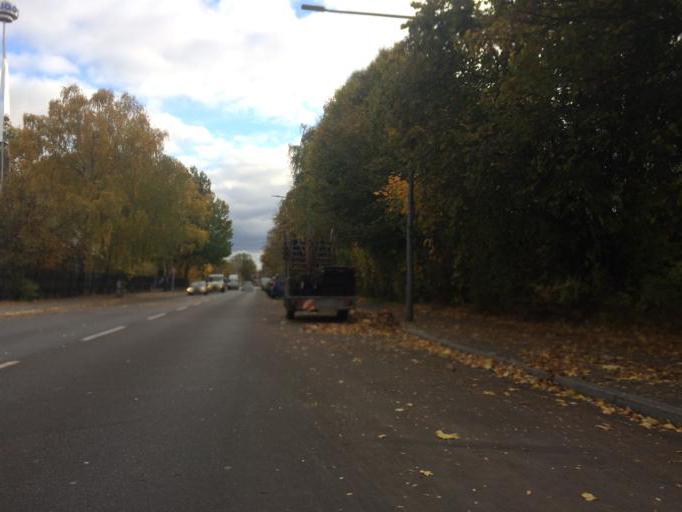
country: DE
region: Berlin
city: Rosenthal
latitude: 52.6010
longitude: 13.3700
